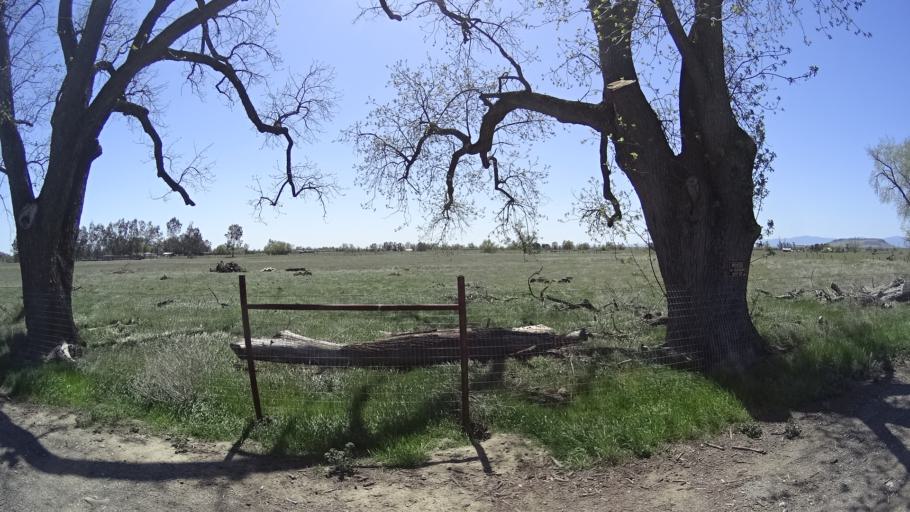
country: US
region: California
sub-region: Glenn County
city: Orland
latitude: 39.7842
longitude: -122.2558
